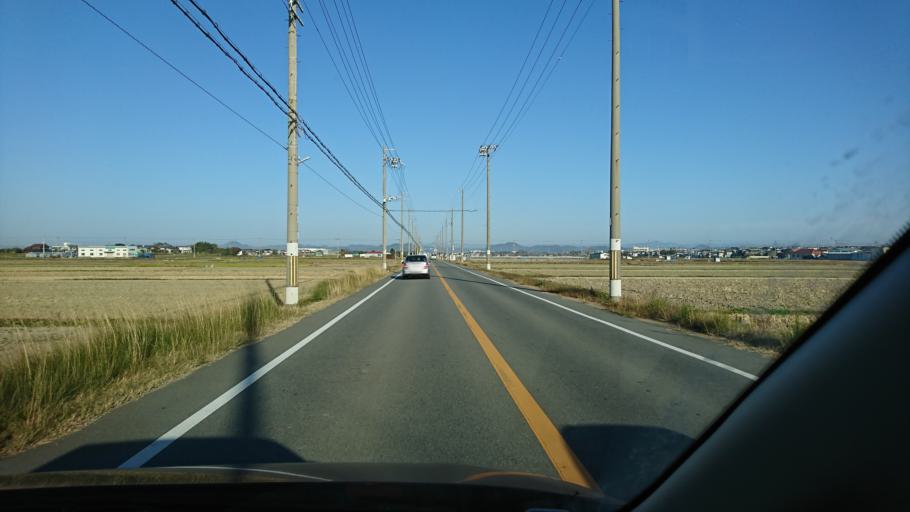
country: JP
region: Hyogo
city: Kakogawacho-honmachi
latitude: 34.7365
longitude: 134.9056
